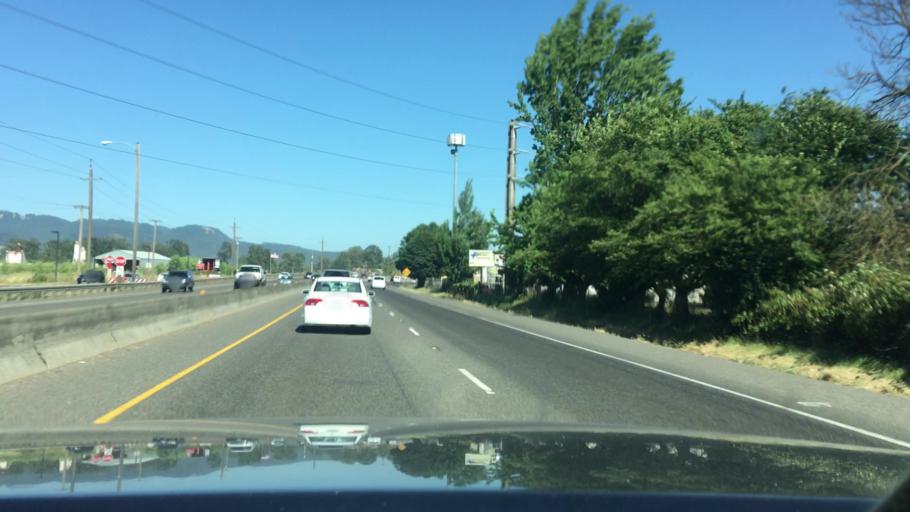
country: US
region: Oregon
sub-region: Lane County
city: Eugene
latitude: 44.0975
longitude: -123.1154
